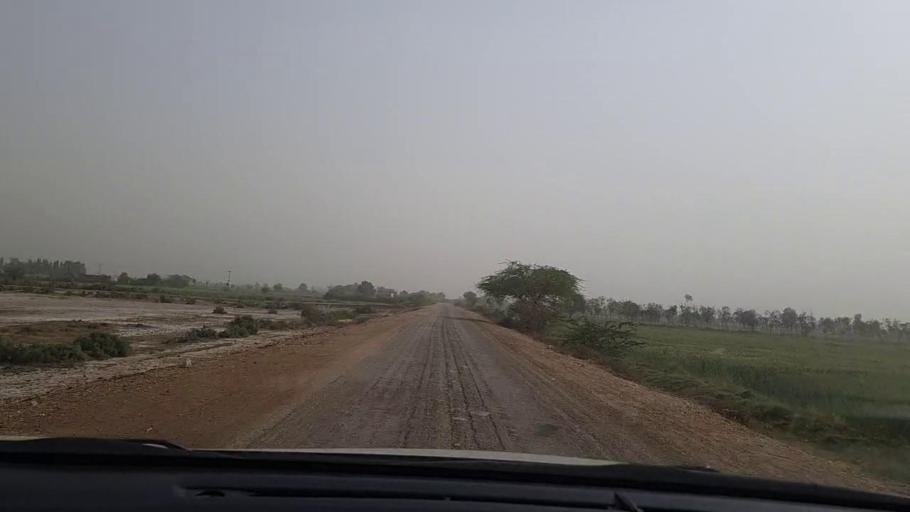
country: PK
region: Sindh
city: Samaro
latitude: 25.3944
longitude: 69.3231
